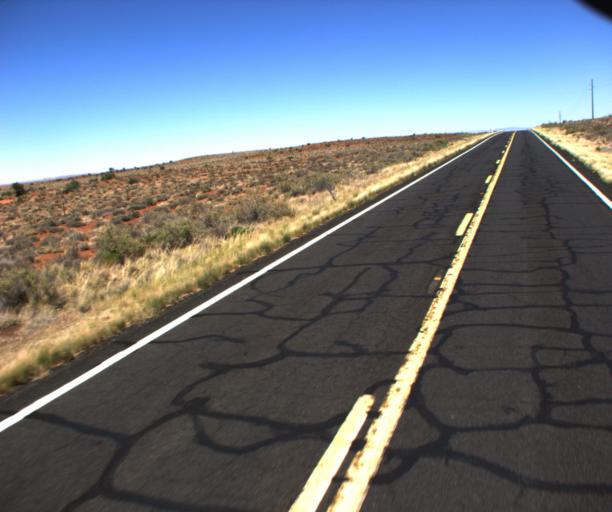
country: US
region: Arizona
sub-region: Coconino County
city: LeChee
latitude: 34.8813
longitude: -110.8840
